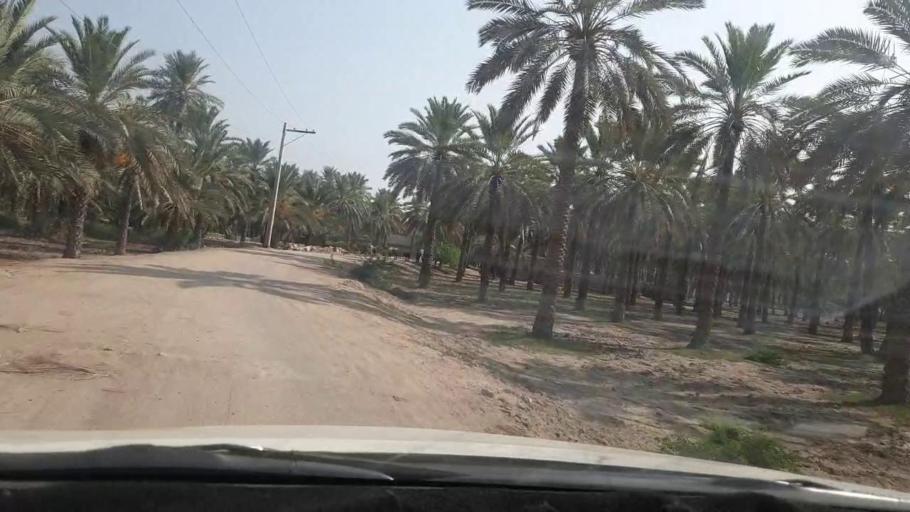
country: PK
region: Sindh
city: Rohri
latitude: 27.5937
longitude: 68.8819
